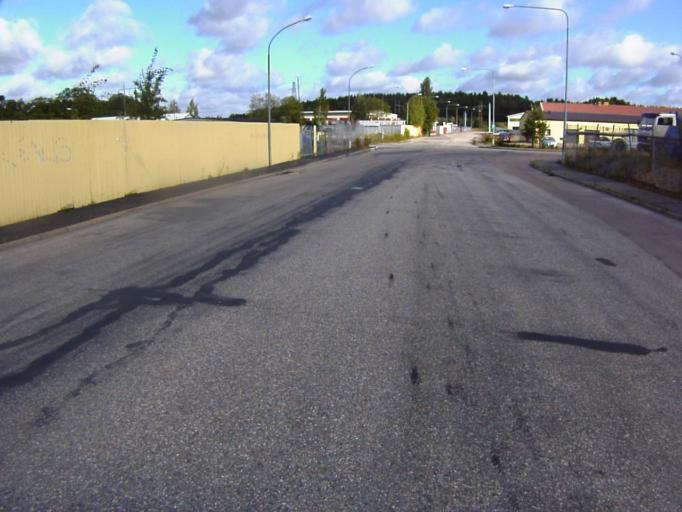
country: SE
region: Soedermanland
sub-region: Eskilstuna Kommun
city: Eskilstuna
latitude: 59.3761
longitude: 16.5752
